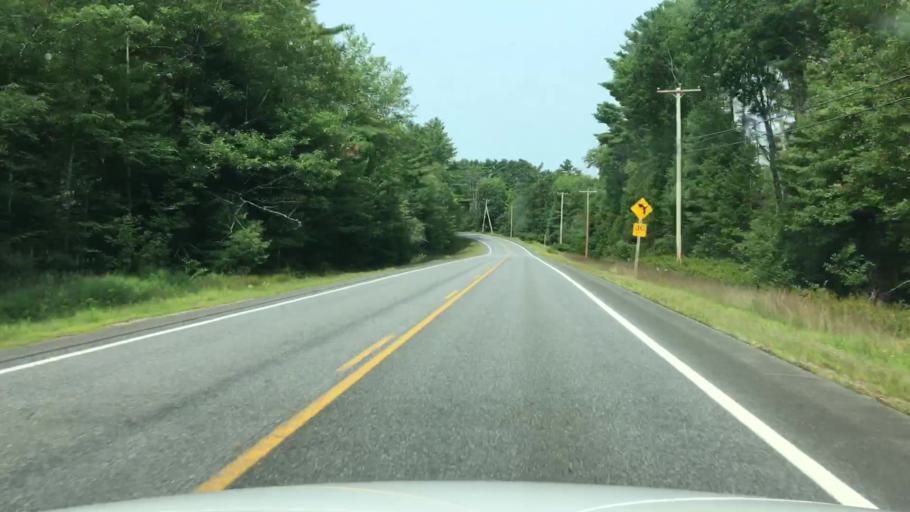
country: US
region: Maine
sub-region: Kennebec County
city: Wayne
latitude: 44.3486
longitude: -70.0469
